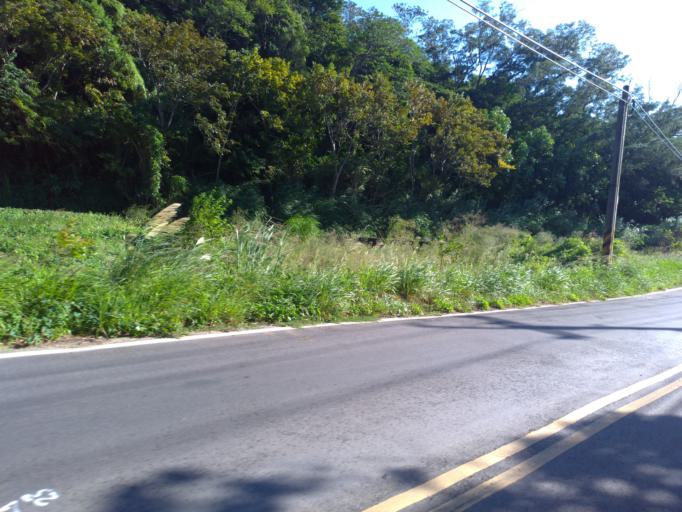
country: TW
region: Taiwan
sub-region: Hsinchu
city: Hsinchu
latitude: 24.7456
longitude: 120.9767
